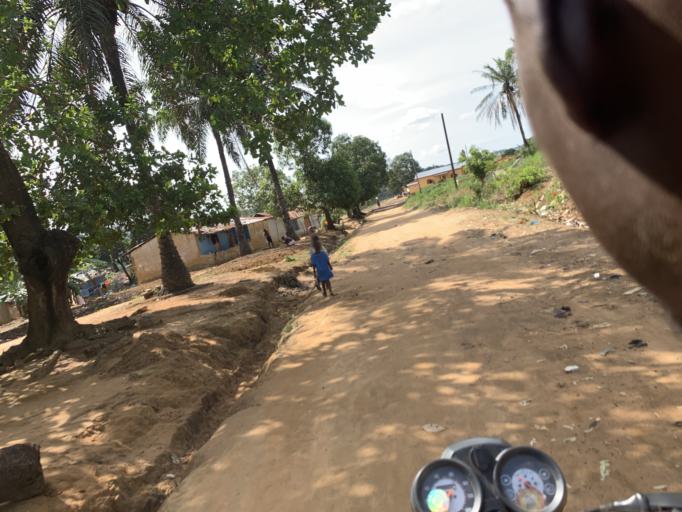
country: SL
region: Western Area
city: Waterloo
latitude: 8.3315
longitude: -13.0642
